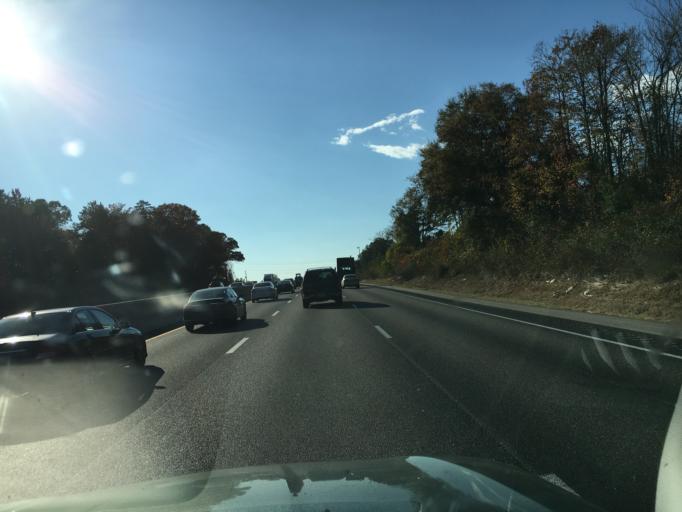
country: US
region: South Carolina
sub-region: Spartanburg County
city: Duncan
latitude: 34.9020
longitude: -82.1309
